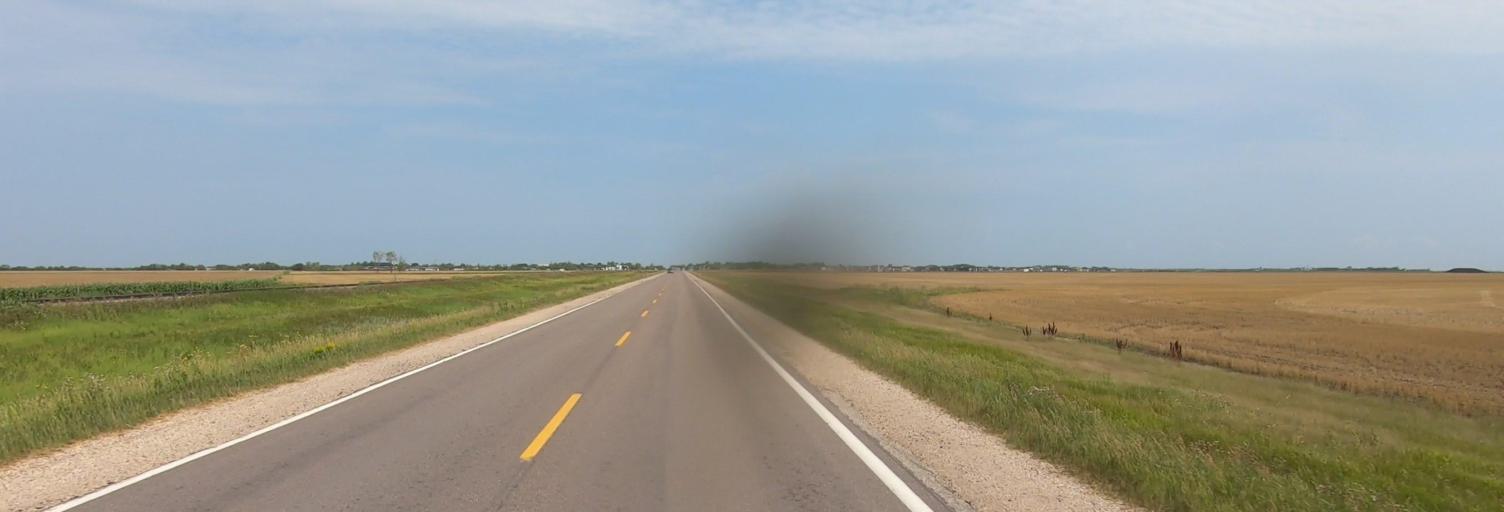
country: CA
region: Manitoba
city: Headingley
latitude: 49.6757
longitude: -97.2765
